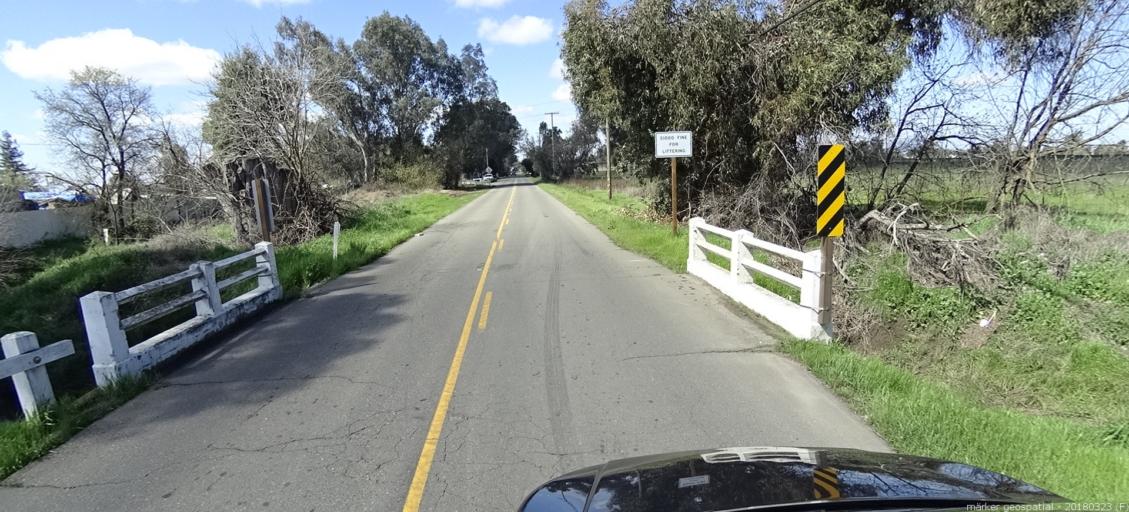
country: US
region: California
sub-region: Sacramento County
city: North Highlands
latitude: 38.6762
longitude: -121.4108
